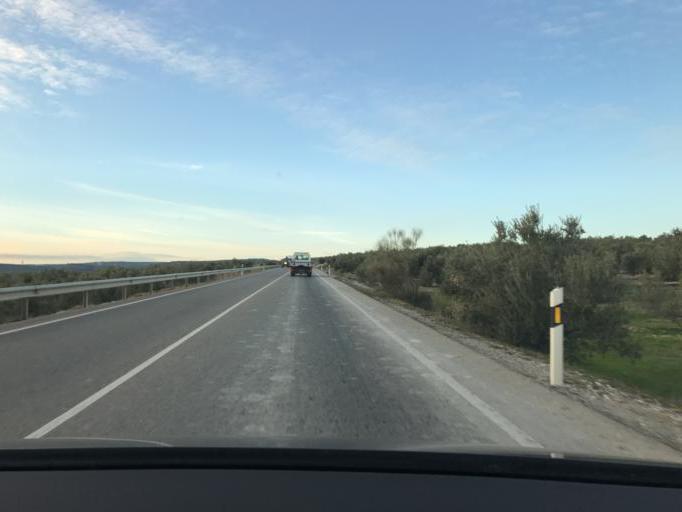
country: ES
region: Andalusia
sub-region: Provincia de Jaen
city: Ubeda
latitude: 37.9750
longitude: -3.3768
